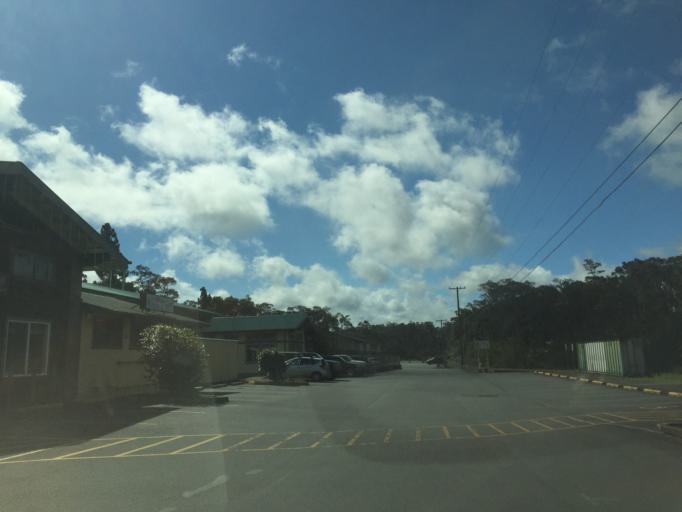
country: US
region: Hawaii
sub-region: Hawaii County
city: Volcano
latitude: 19.4292
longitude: -155.2329
